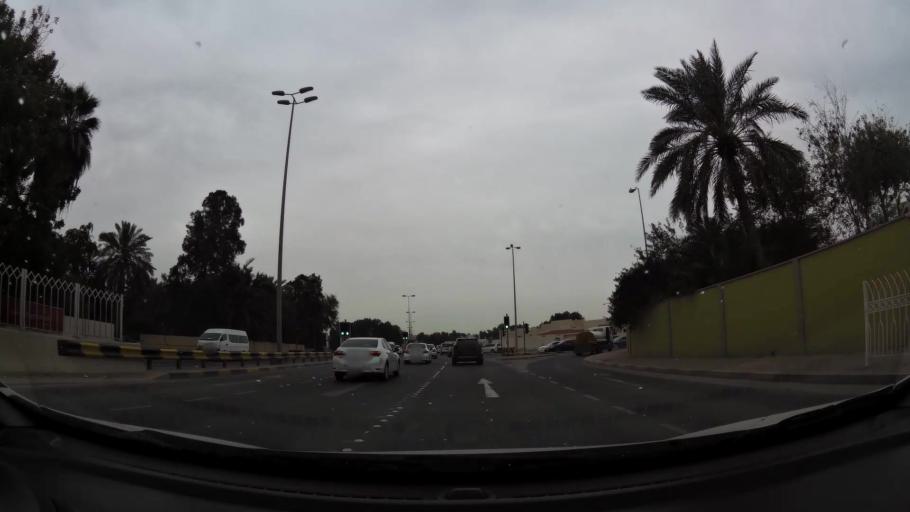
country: BH
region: Manama
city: Jidd Hafs
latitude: 26.2097
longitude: 50.5340
